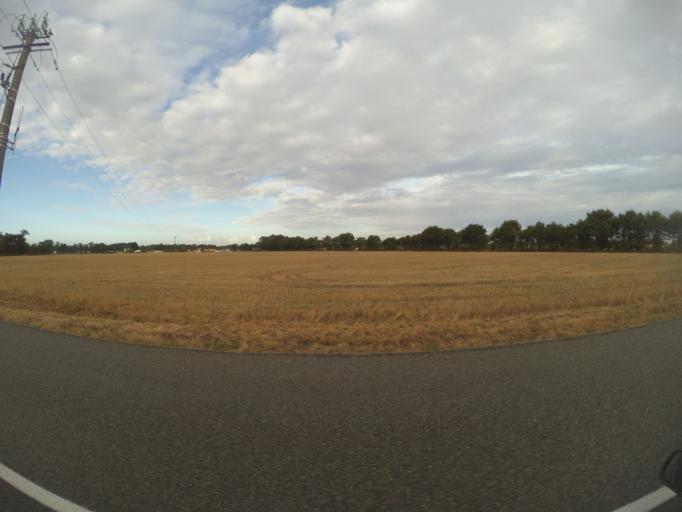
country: FR
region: Pays de la Loire
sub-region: Departement de la Loire-Atlantique
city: La Planche
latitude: 47.0160
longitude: -1.4237
